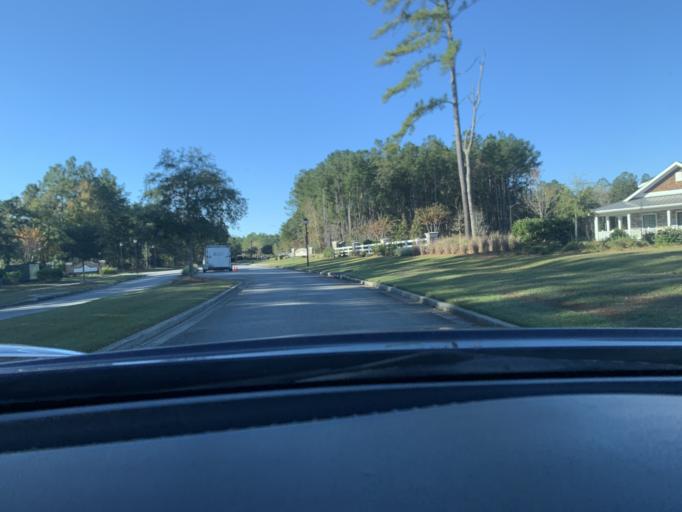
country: US
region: Georgia
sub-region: Chatham County
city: Pooler
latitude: 32.0679
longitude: -81.2713
